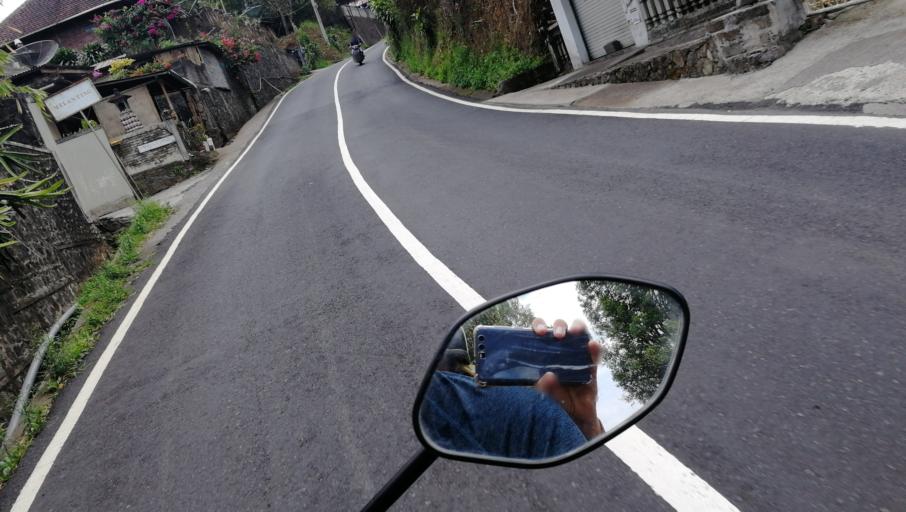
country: ID
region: Bali
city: Munduk
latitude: -8.2621
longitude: 115.0656
